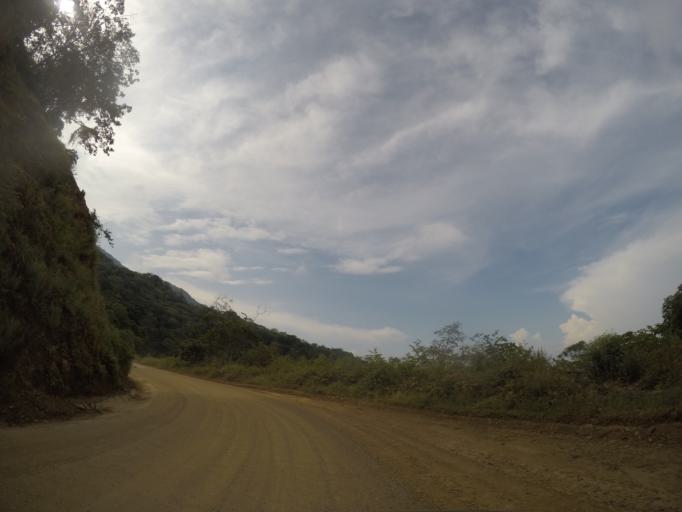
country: MX
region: Oaxaca
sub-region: San Pedro Pochutla
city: Los Naranjos Esquipulas
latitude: 15.9568
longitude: -96.4521
